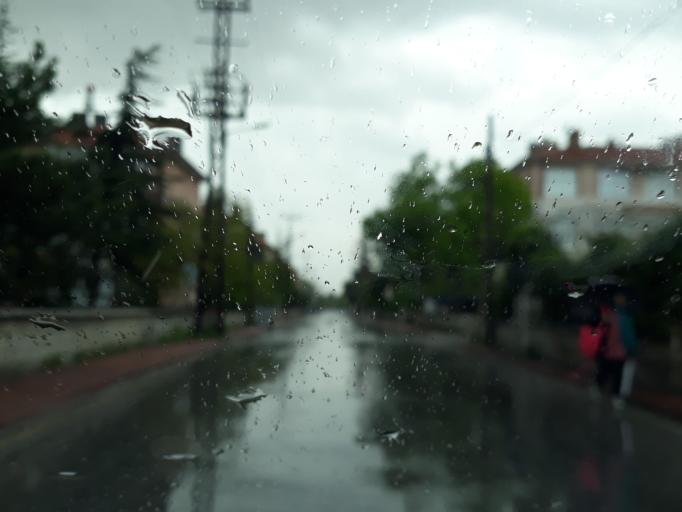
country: TR
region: Konya
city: Selcuklu
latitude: 37.9139
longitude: 32.4956
